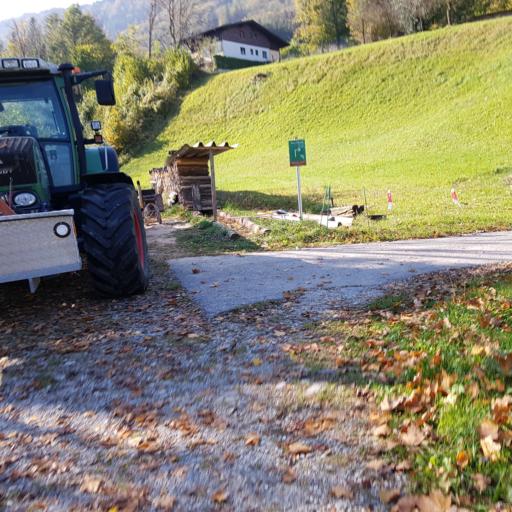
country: AT
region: Salzburg
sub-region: Politischer Bezirk Hallein
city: Hallein
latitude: 47.6631
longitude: 13.1164
